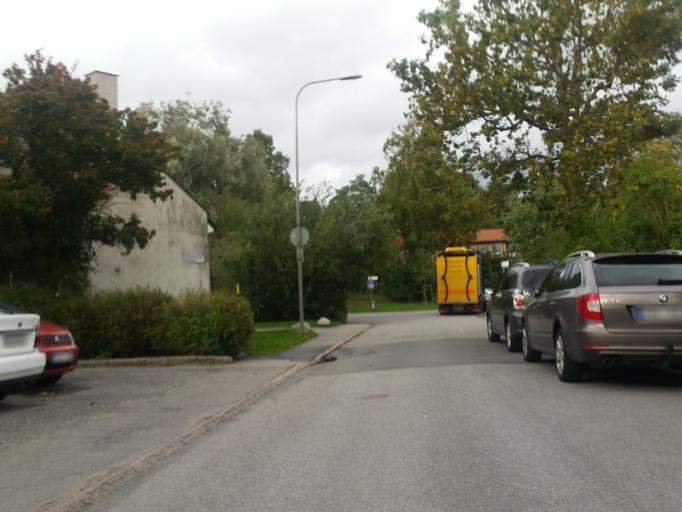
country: SE
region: Stockholm
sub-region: Stockholms Kommun
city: Arsta
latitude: 59.2559
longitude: 18.0951
